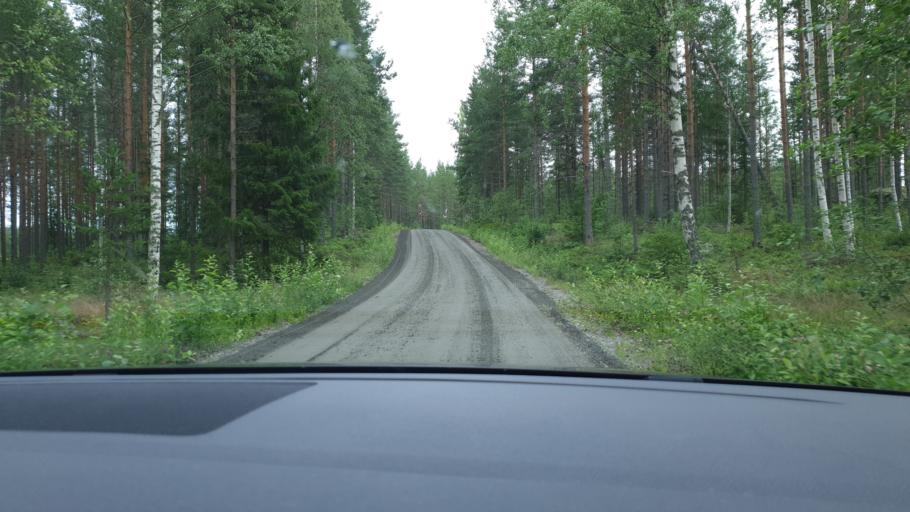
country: SE
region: Gaevleborg
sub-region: Hudiksvalls Kommun
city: Iggesund
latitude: 61.5305
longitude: 17.0118
